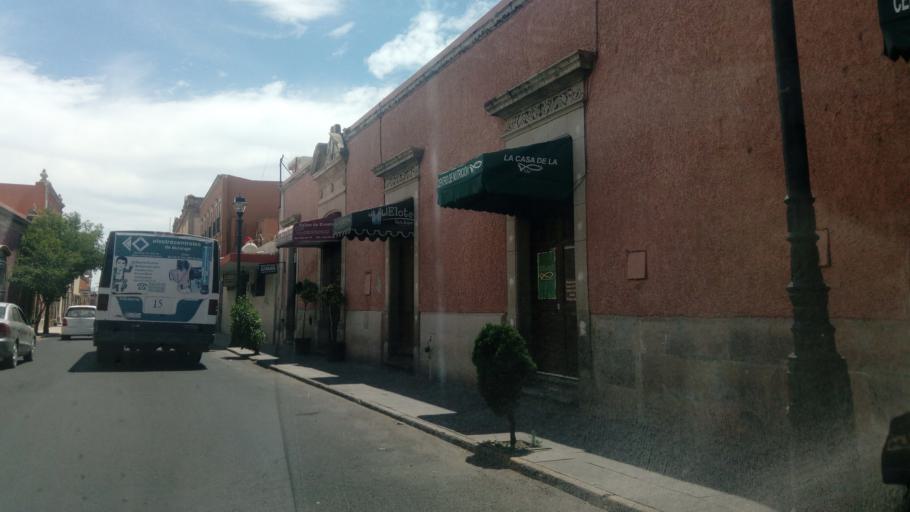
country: MX
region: Durango
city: Victoria de Durango
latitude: 24.0254
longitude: -104.6721
